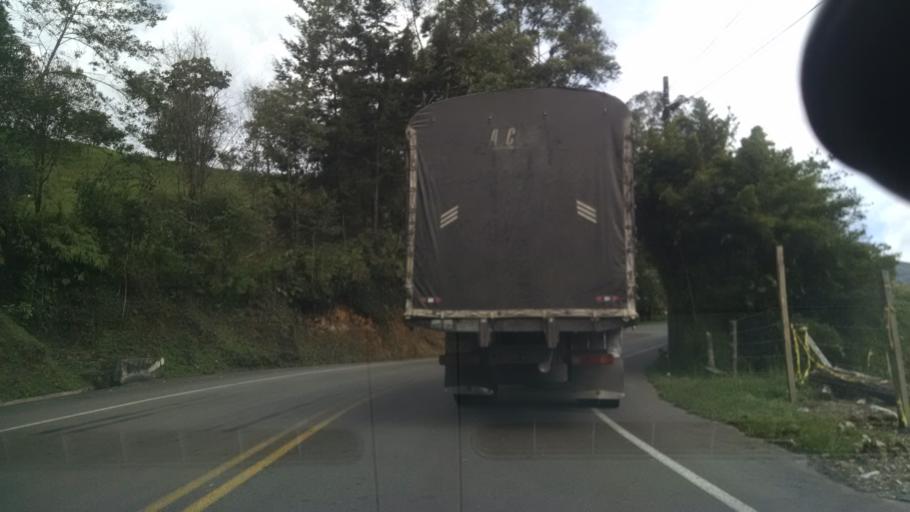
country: CO
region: Antioquia
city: Caldas
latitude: 6.0337
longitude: -75.6247
